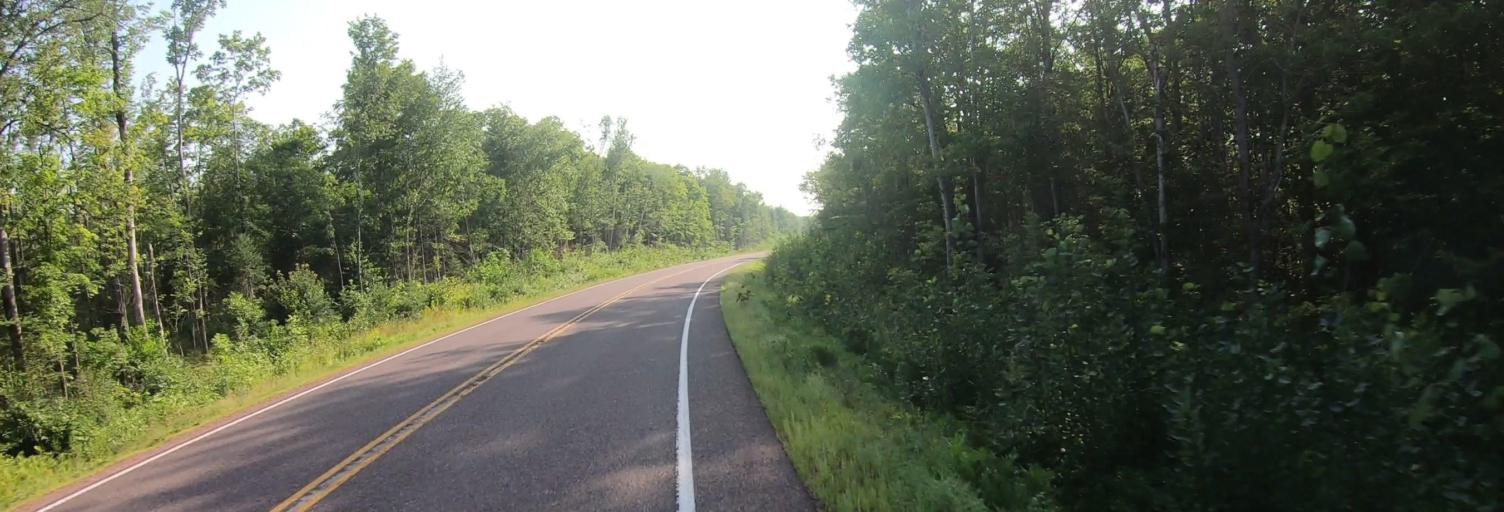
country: US
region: Wisconsin
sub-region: Ashland County
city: Ashland
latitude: 46.3000
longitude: -90.7873
